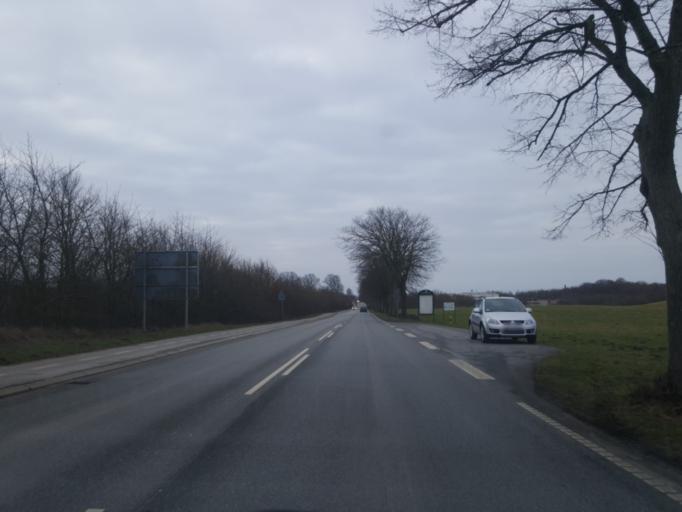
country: DK
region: Zealand
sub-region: Vordingborg Kommune
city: Vordingborg
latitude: 55.0187
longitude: 11.9273
